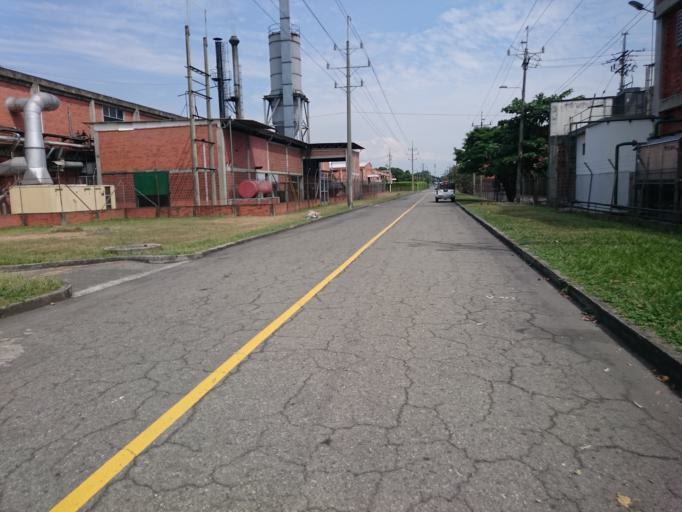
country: CO
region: Cauca
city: Puerto Tejada
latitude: 3.2026
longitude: -76.4161
